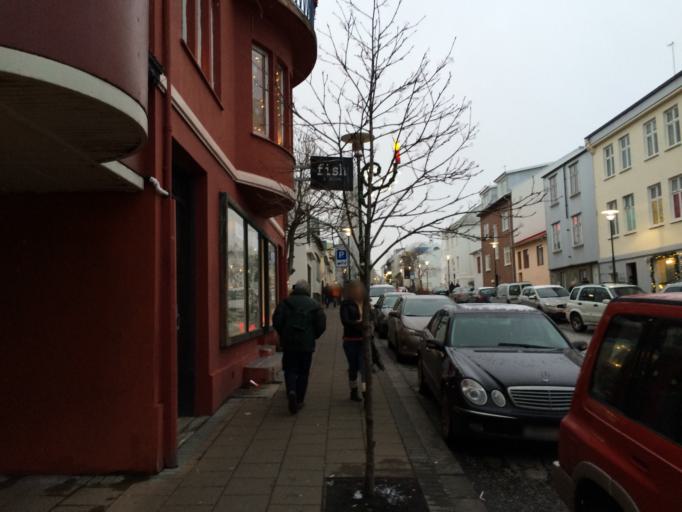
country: IS
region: Capital Region
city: Reykjavik
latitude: 64.1442
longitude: -21.9301
